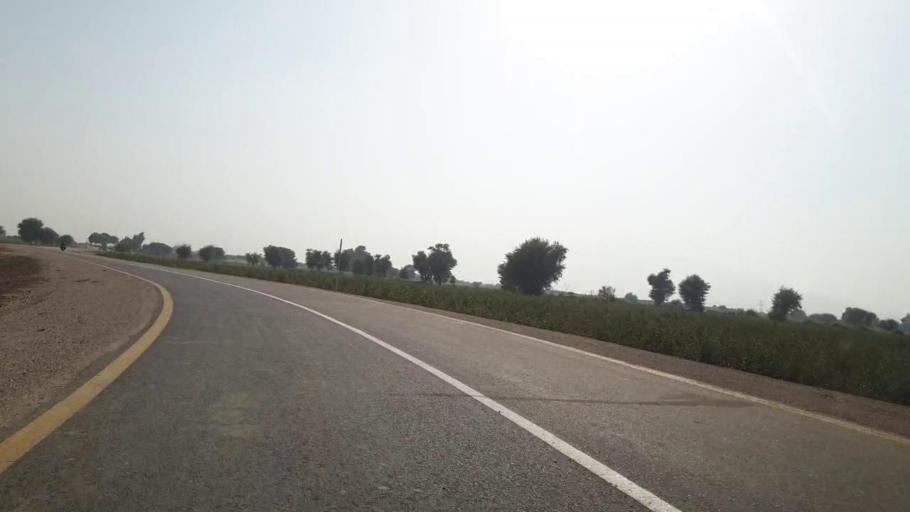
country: PK
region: Sindh
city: Bhan
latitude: 26.5062
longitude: 67.7833
